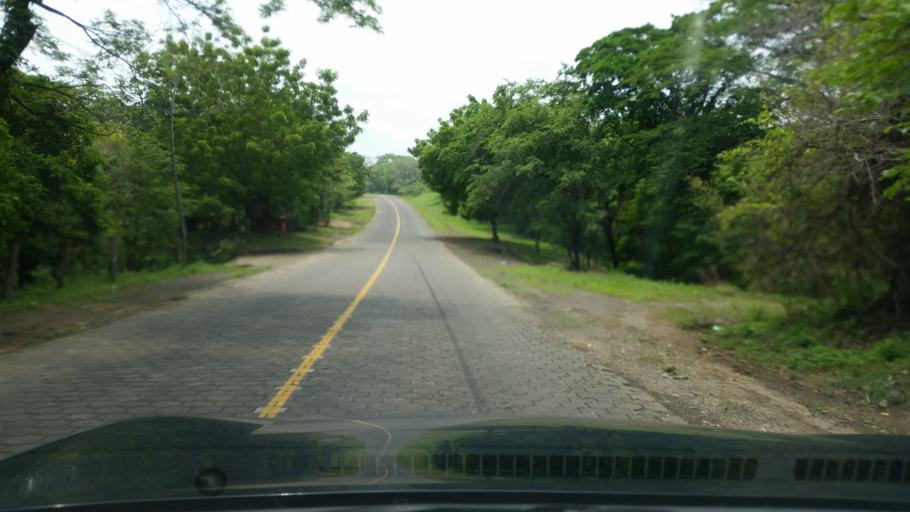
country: NI
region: Managua
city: Carlos Fonseca Amador
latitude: 11.9341
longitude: -86.5071
